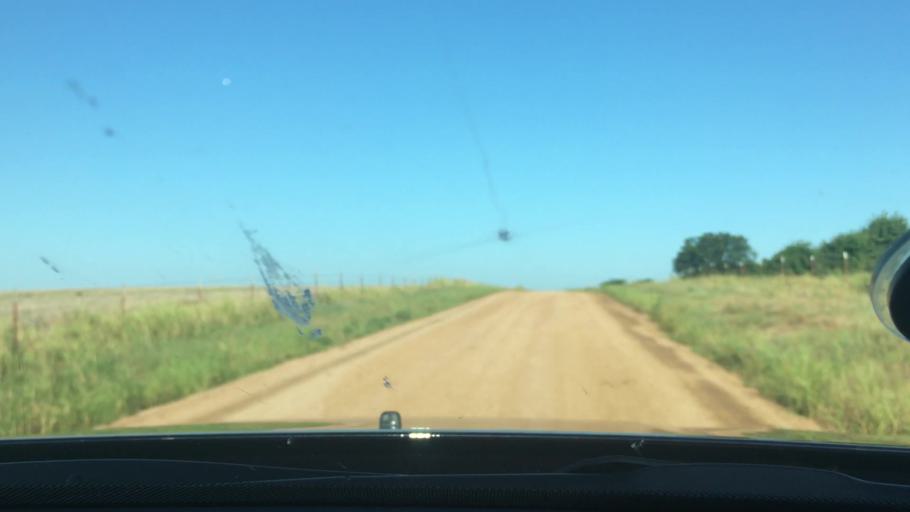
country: US
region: Oklahoma
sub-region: Murray County
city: Sulphur
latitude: 34.4194
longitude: -96.7873
